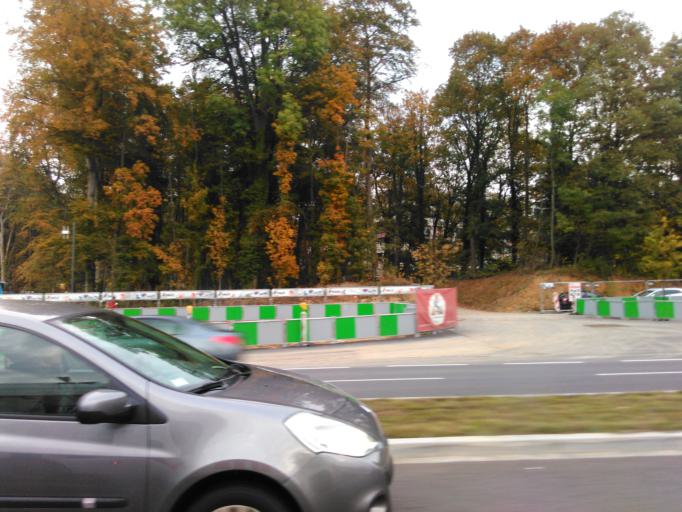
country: LU
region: Luxembourg
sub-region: Canton de Luxembourg
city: Luxembourg
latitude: 49.6185
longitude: 6.1372
